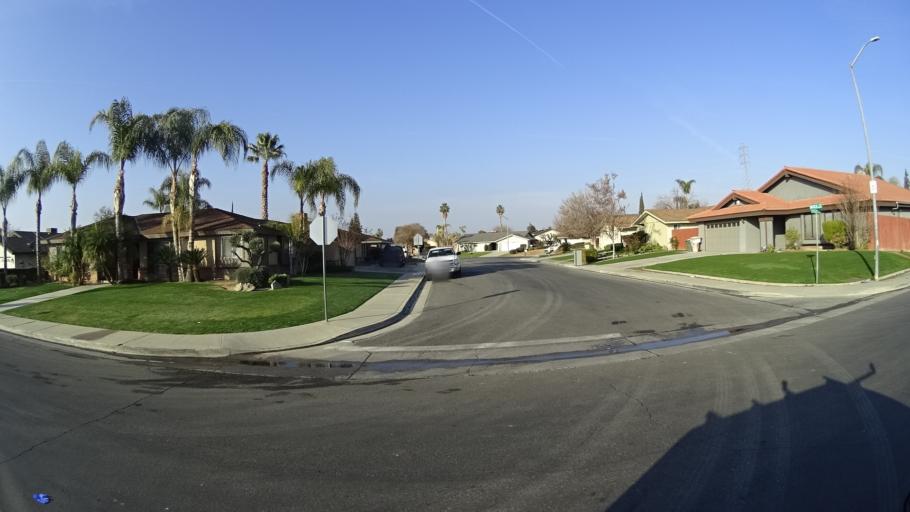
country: US
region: California
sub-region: Kern County
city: Oildale
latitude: 35.4011
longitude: -118.9387
